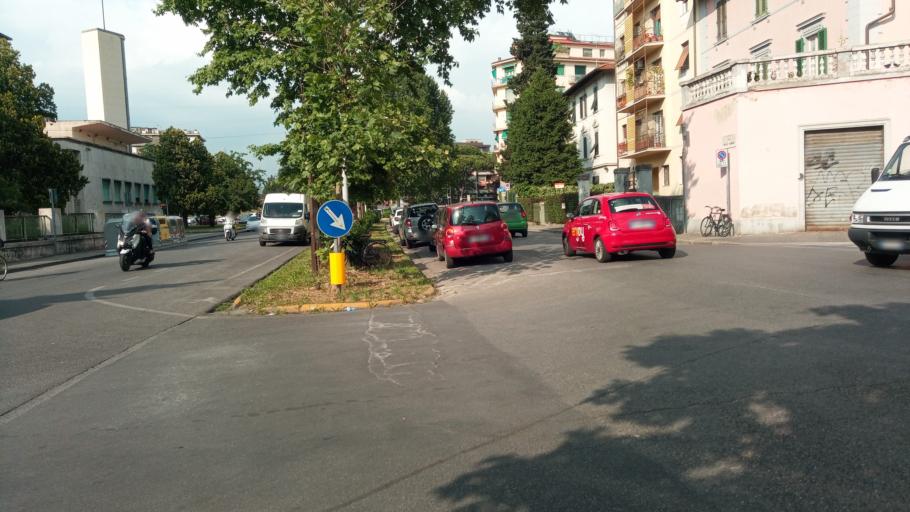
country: IT
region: Tuscany
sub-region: Province of Florence
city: Florence
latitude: 43.7855
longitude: 11.2251
